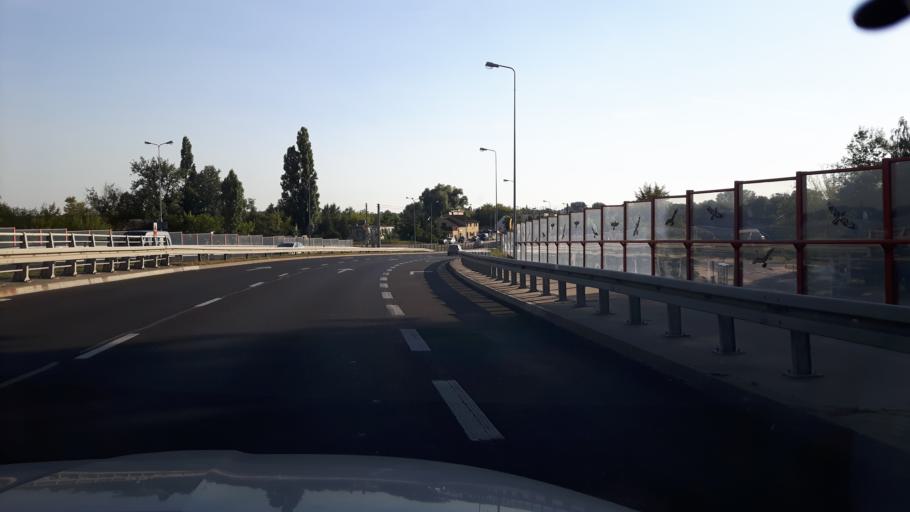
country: PL
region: Masovian Voivodeship
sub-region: Powiat legionowski
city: Nieporet
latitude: 52.4555
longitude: 21.0158
